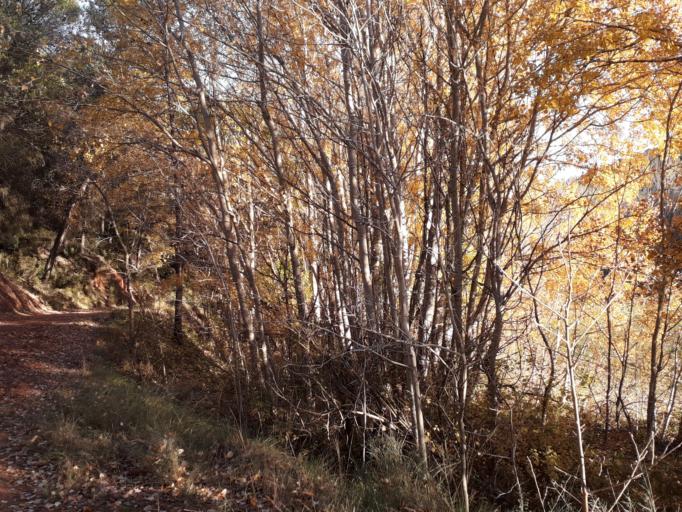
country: ES
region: Catalonia
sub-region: Provincia de Barcelona
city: Sant Marti de Tous
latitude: 41.5120
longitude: 1.5155
